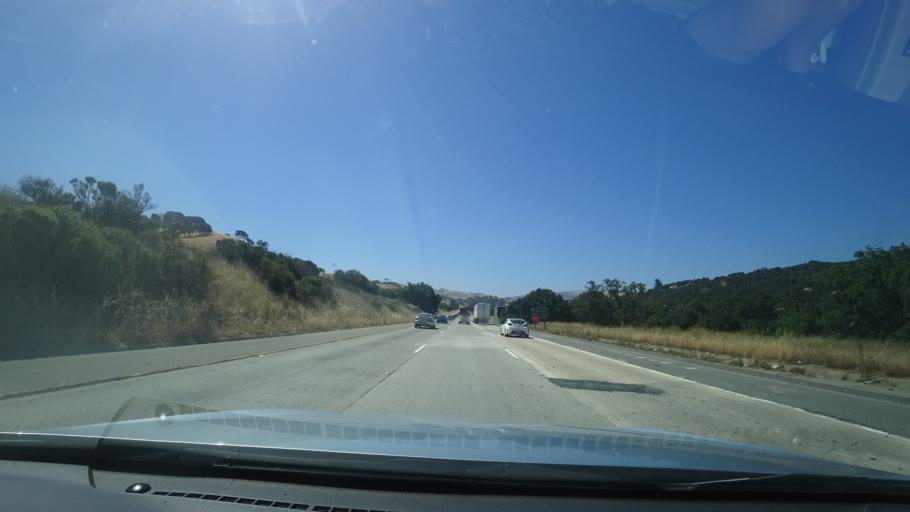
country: US
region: California
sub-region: Alameda County
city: Pleasanton
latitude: 37.6192
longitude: -121.8789
